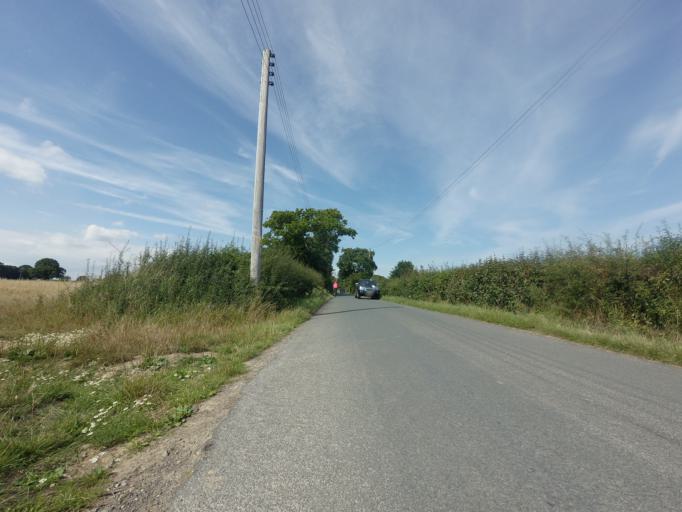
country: GB
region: England
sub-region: East Sussex
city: Rye
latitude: 50.9758
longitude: 0.7401
